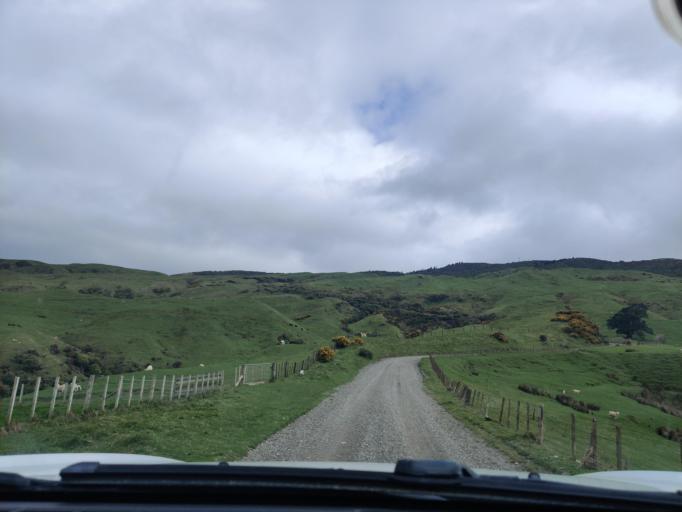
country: NZ
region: Manawatu-Wanganui
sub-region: Palmerston North City
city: Palmerston North
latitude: -40.2815
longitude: 175.8568
